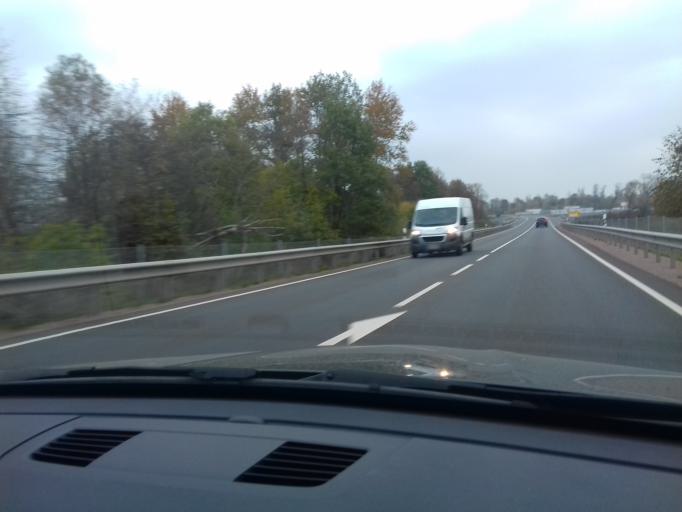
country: DE
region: Rheinland-Pfalz
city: Wasserliesch
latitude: 49.6925
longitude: 6.5531
